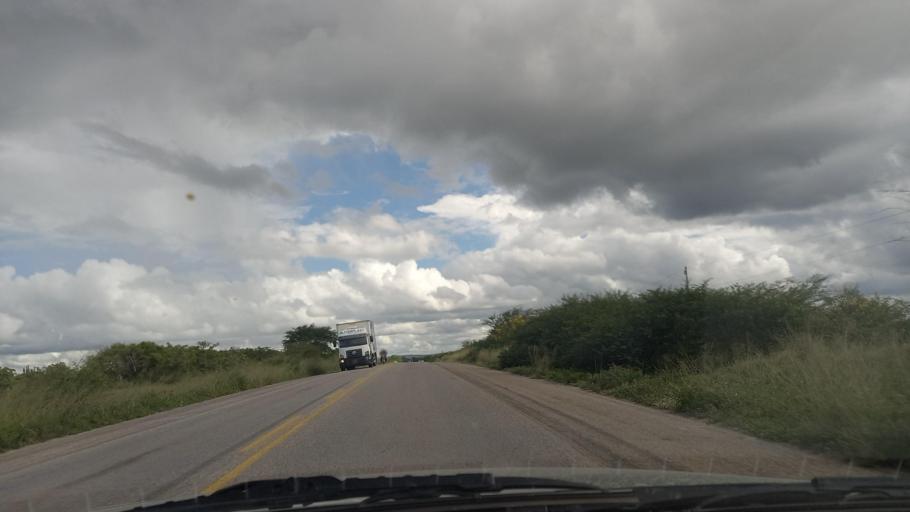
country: BR
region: Pernambuco
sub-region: Cachoeirinha
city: Cachoeirinha
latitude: -8.5202
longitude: -36.2573
